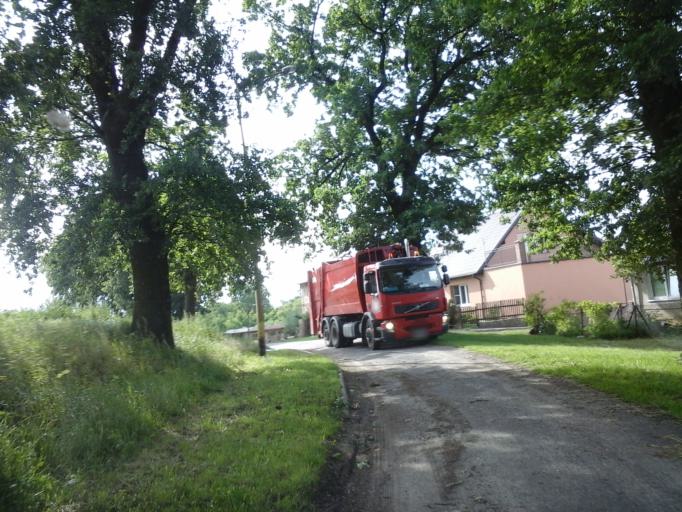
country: PL
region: West Pomeranian Voivodeship
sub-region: Powiat choszczenski
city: Krzecin
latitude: 53.1029
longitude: 15.5447
